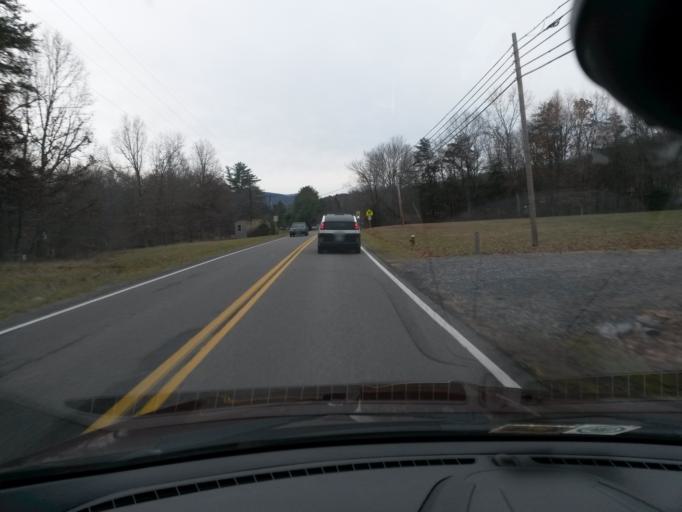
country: US
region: Virginia
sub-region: Alleghany County
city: Clifton Forge
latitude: 37.8126
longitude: -79.7429
